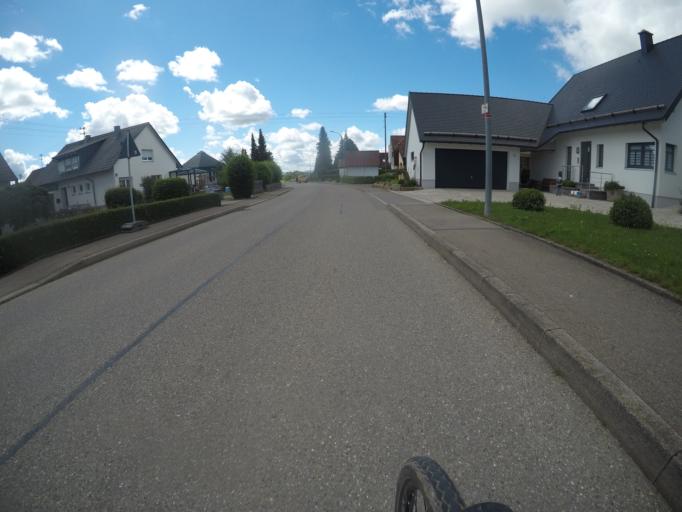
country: DE
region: Baden-Wuerttemberg
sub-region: Regierungsbezirk Stuttgart
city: Motzingen
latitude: 48.5110
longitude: 8.7440
